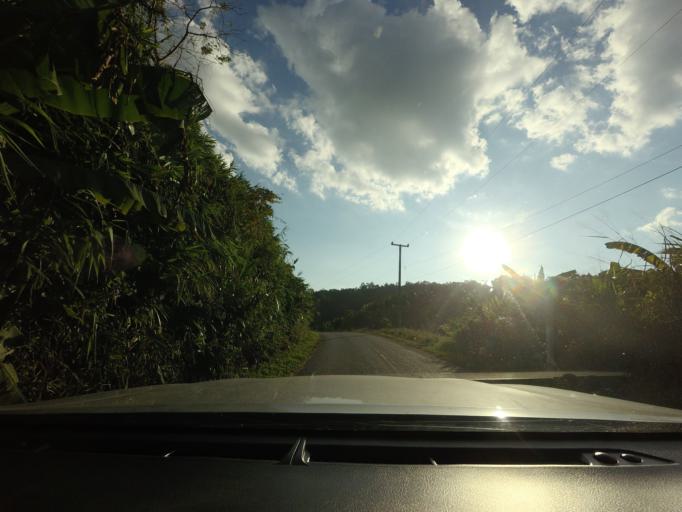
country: TH
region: Chiang Mai
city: Phrao
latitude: 19.5225
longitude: 99.1643
